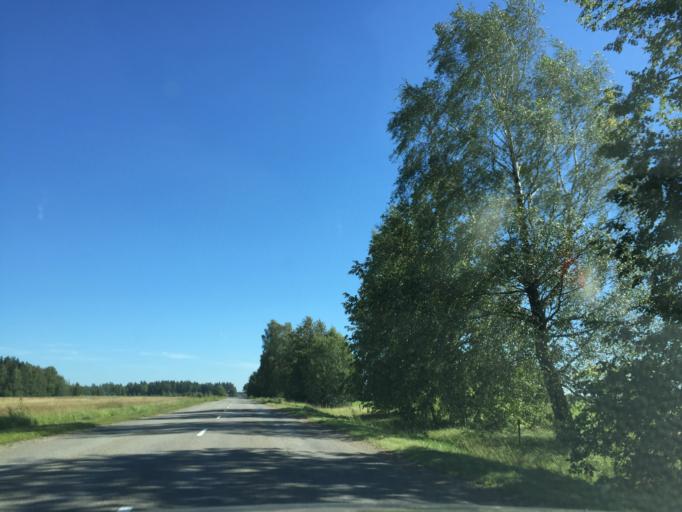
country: LV
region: Akniste
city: Akniste
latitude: 56.1503
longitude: 25.7797
